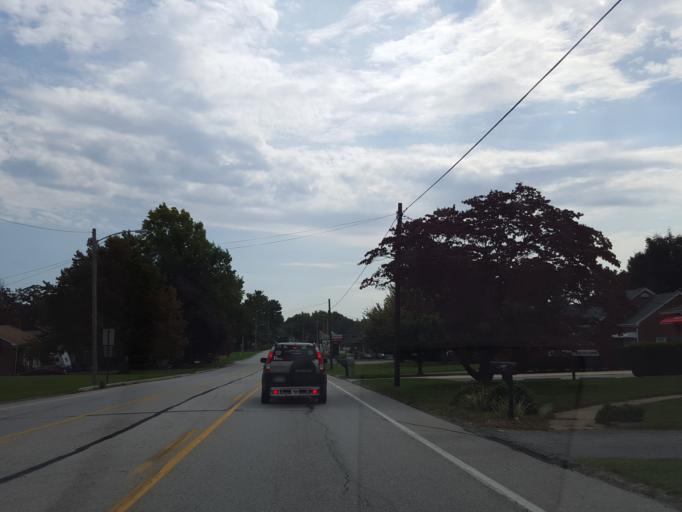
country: US
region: Pennsylvania
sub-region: York County
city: Spry
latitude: 39.9277
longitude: -76.6865
